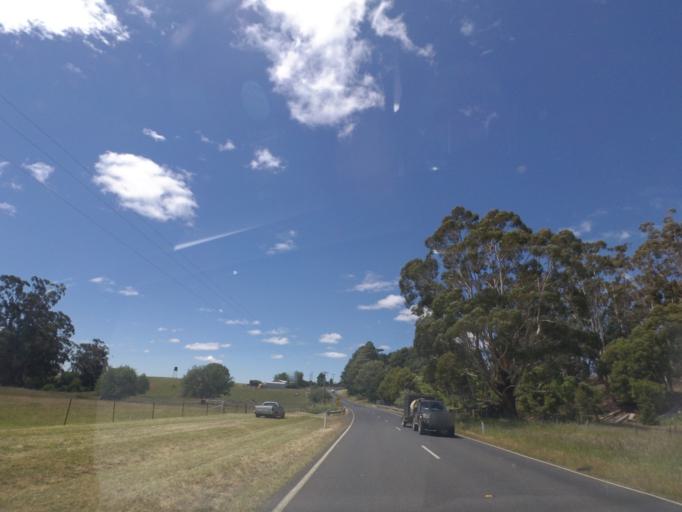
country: AU
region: Victoria
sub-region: Mount Alexander
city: Castlemaine
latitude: -37.3255
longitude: 144.1929
